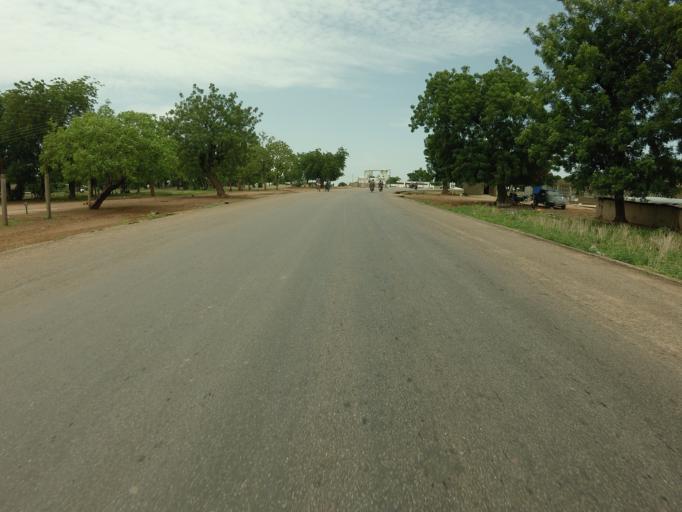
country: GH
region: Upper East
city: Bawku
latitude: 11.0701
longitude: -0.2051
